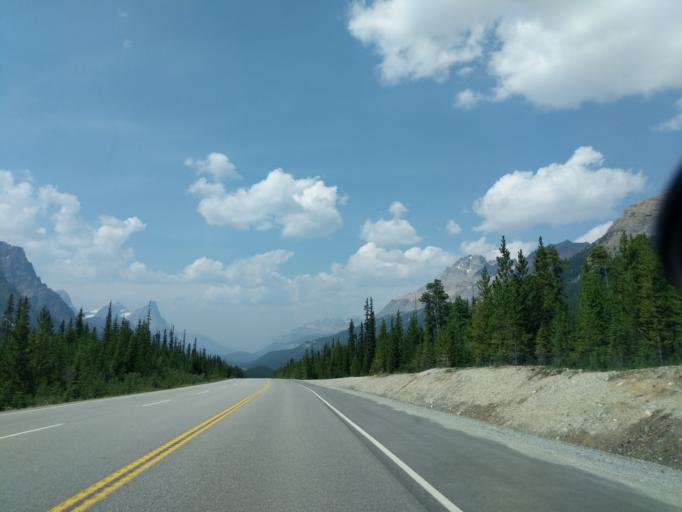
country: CA
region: Alberta
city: Lake Louise
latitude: 51.7346
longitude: -116.5058
